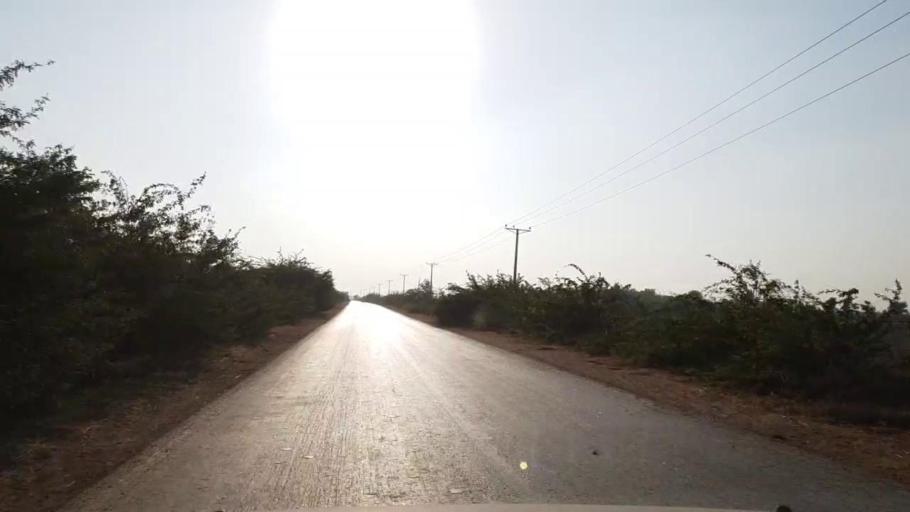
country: PK
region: Sindh
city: Bulri
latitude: 24.8051
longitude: 68.3125
